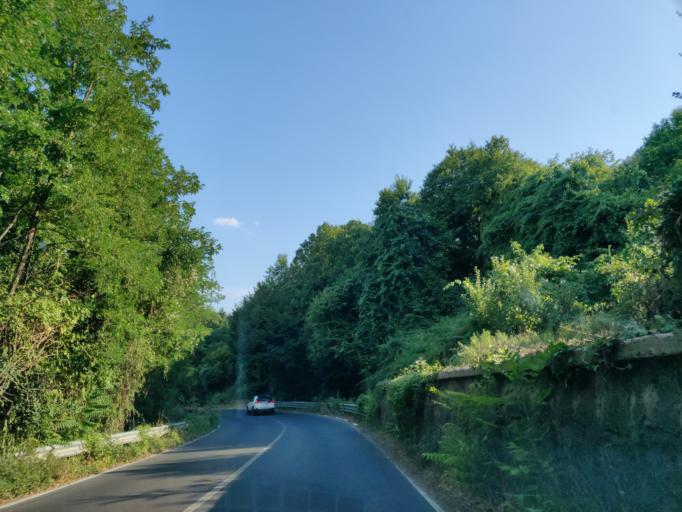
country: IT
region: Latium
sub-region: Provincia di Viterbo
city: Acquapendente
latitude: 42.7514
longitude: 11.8632
